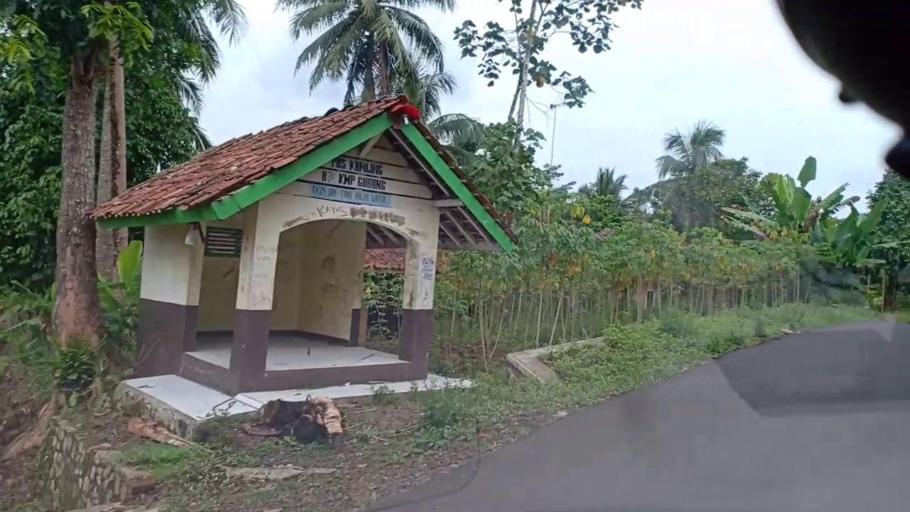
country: ID
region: West Java
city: Tangsi
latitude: -7.3376
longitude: 108.3033
